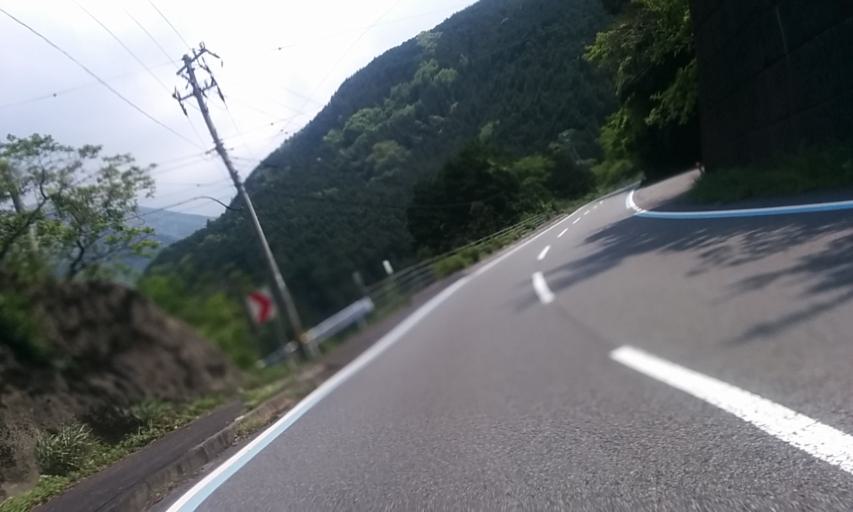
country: JP
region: Ehime
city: Saijo
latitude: 33.8506
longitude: 133.2061
